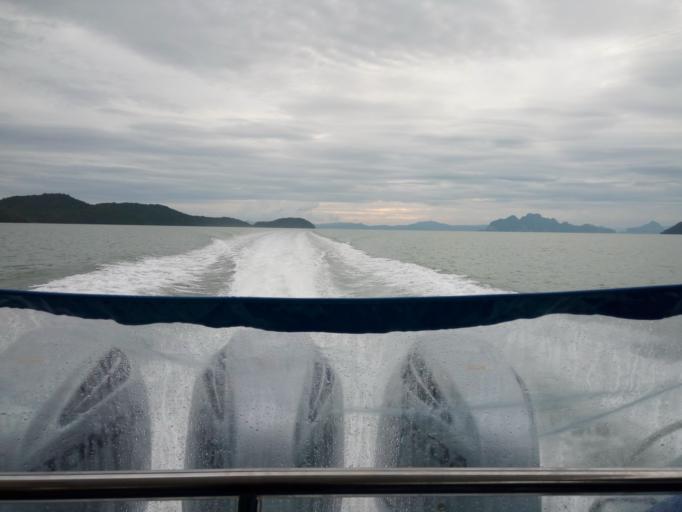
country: TH
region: Phangnga
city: Ko Yao
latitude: 8.1009
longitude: 98.5625
